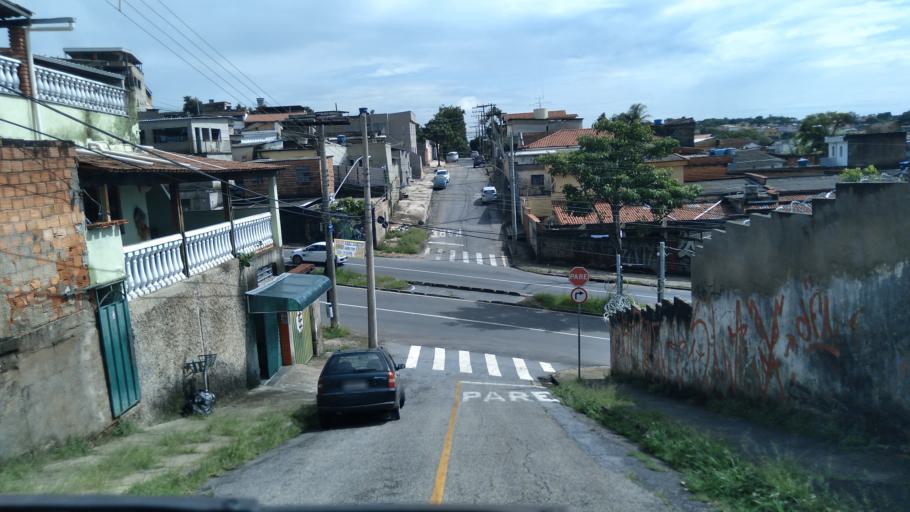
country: BR
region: Minas Gerais
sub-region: Contagem
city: Contagem
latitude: -19.9252
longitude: -44.0030
